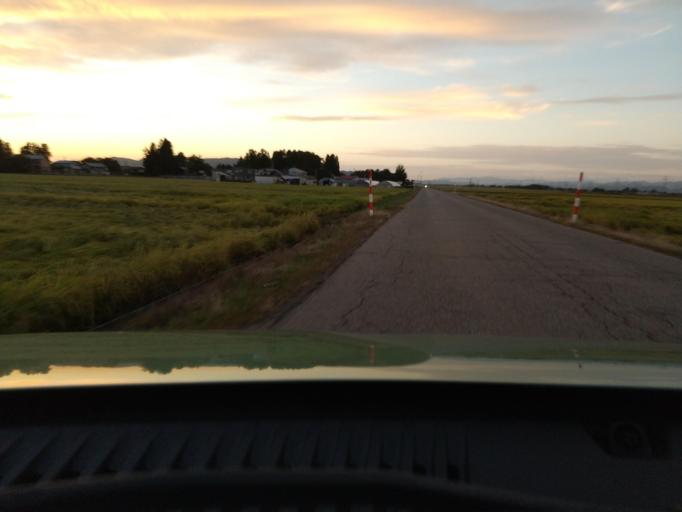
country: JP
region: Akita
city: Omagari
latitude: 39.4041
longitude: 140.5033
